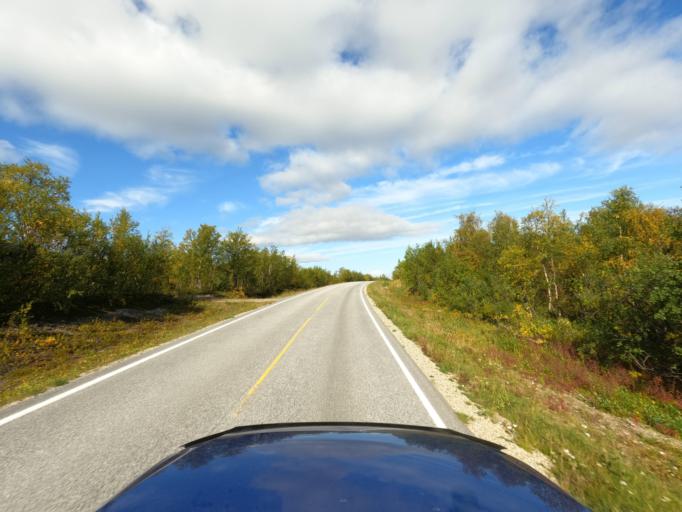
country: NO
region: Finnmark Fylke
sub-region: Karasjok
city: Karasjohka
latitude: 69.6157
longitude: 25.3012
